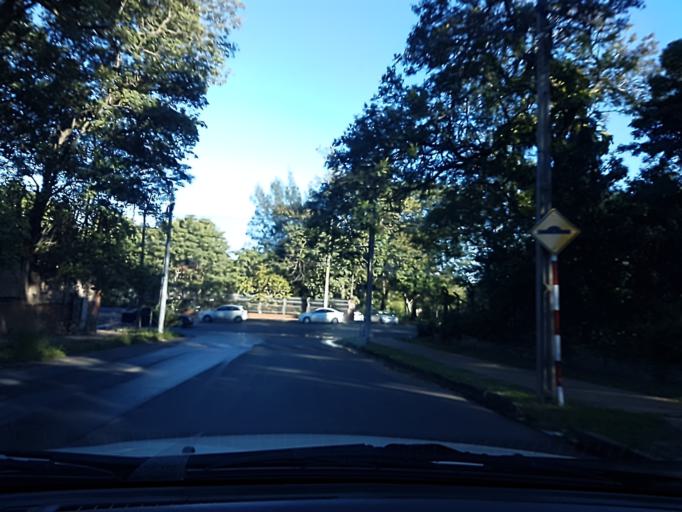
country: PY
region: Asuncion
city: Asuncion
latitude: -25.2801
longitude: -57.5862
